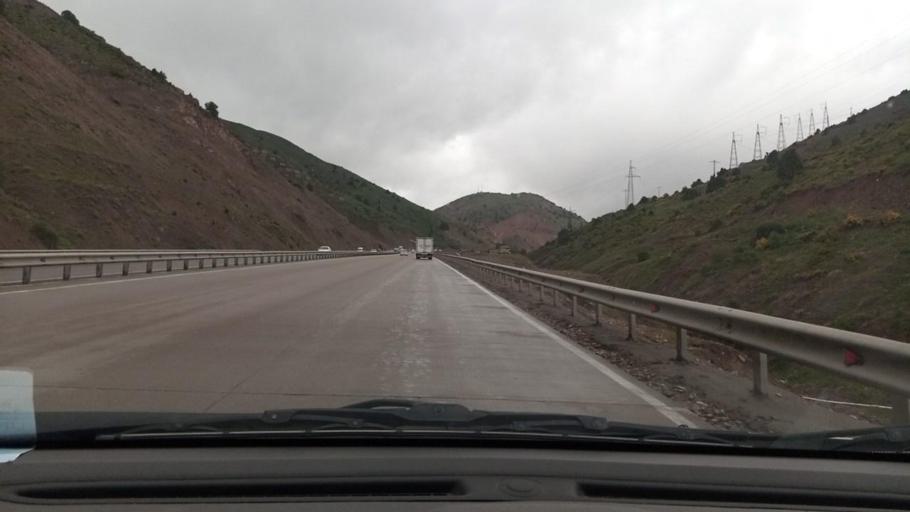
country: UZ
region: Toshkent
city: Angren
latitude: 41.0556
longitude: 70.5646
